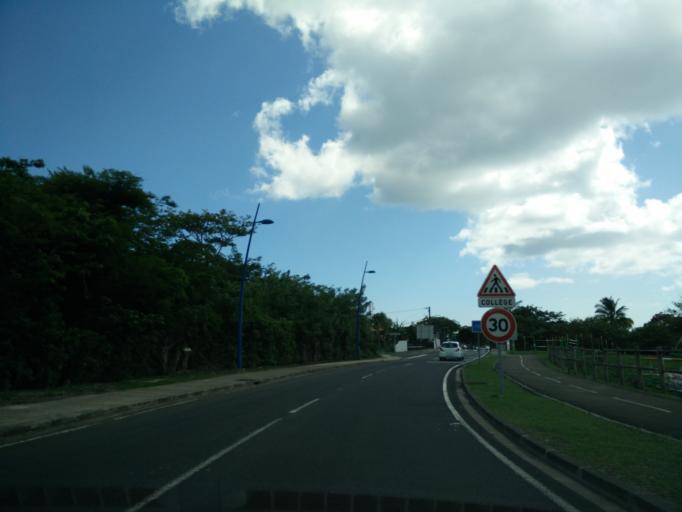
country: MQ
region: Martinique
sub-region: Martinique
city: Les Trois-Ilets
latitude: 14.4938
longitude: -61.0776
